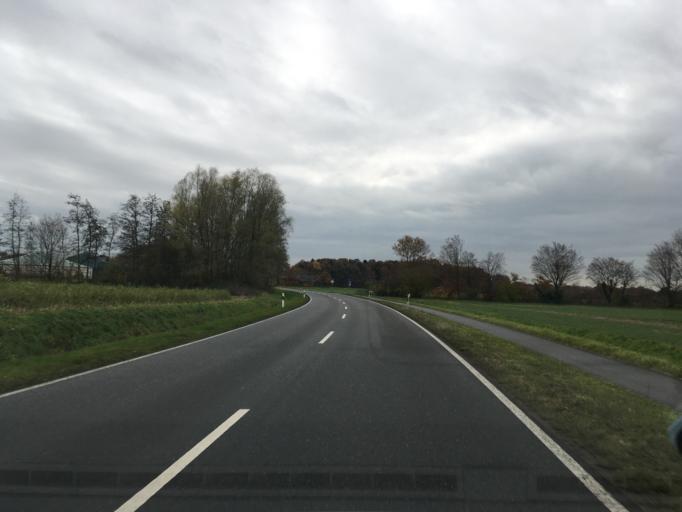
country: DE
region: North Rhine-Westphalia
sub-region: Regierungsbezirk Munster
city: Gescher
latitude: 51.9846
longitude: 7.0281
